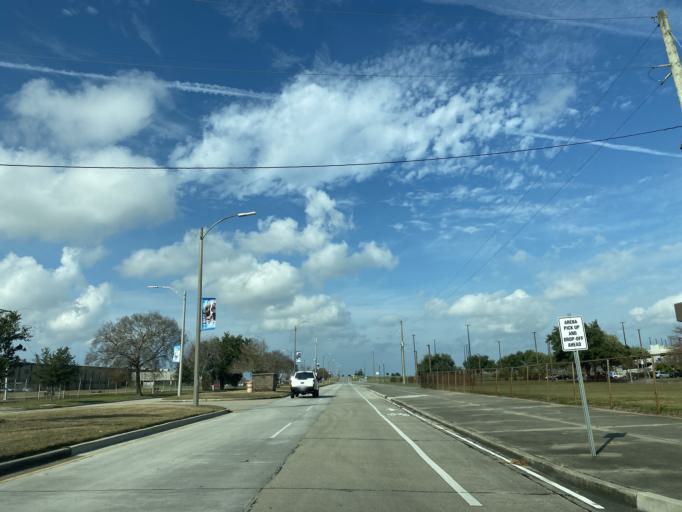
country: US
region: Louisiana
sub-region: Orleans Parish
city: New Orleans
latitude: 30.0286
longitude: -90.0522
